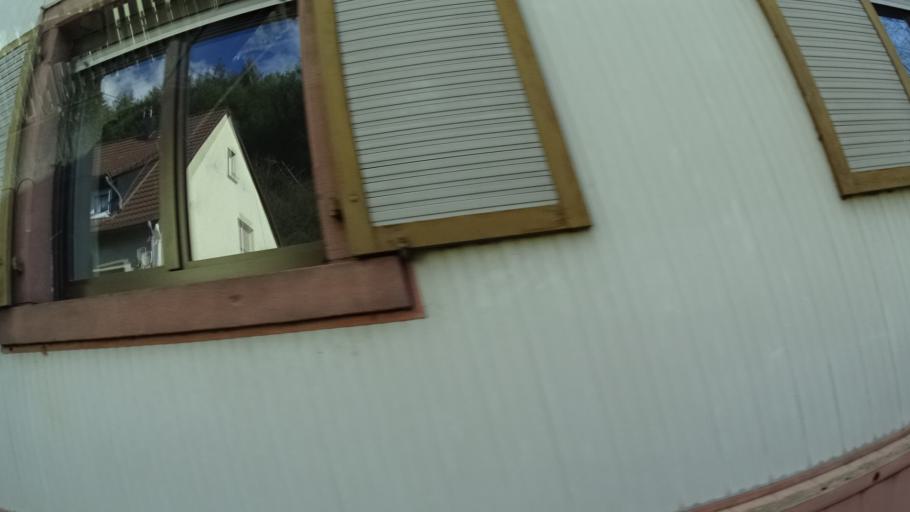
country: DE
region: Rheinland-Pfalz
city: Otzweiler
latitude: 49.7141
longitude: 7.5129
